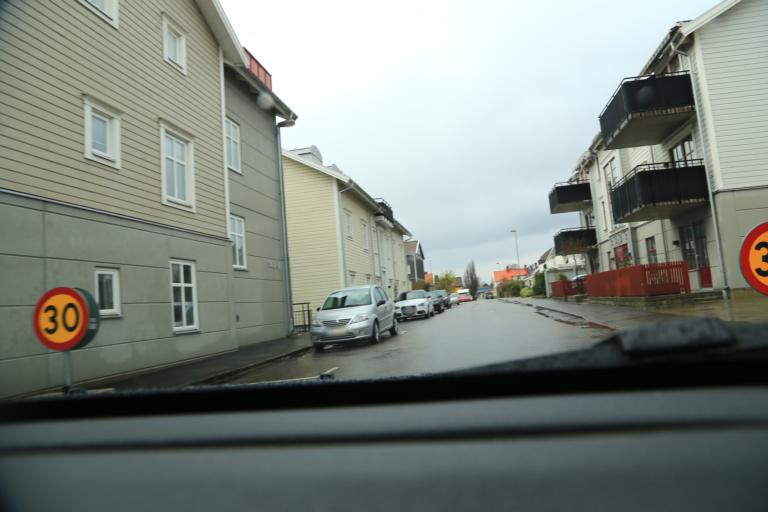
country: SE
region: Halland
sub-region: Varbergs Kommun
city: Varberg
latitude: 57.1078
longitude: 12.2602
